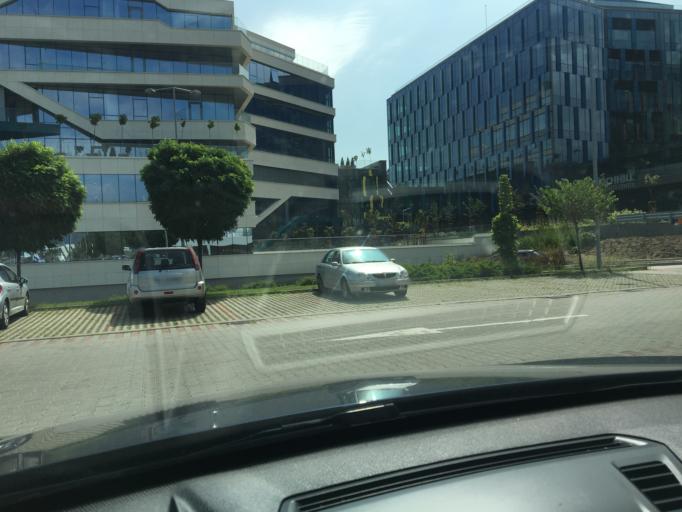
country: BG
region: Sofia-Capital
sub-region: Stolichna Obshtina
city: Sofia
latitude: 42.6229
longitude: 23.3674
